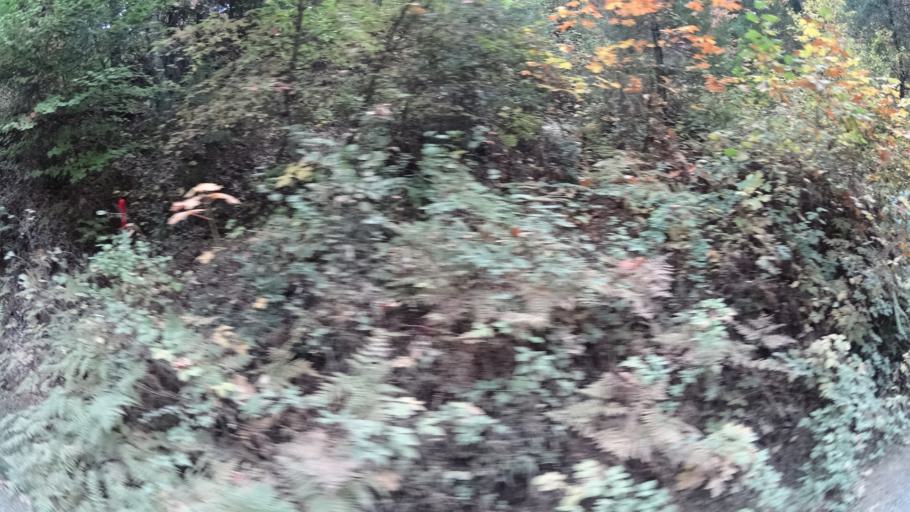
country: US
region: California
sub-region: Siskiyou County
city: Happy Camp
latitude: 41.7910
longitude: -123.3384
